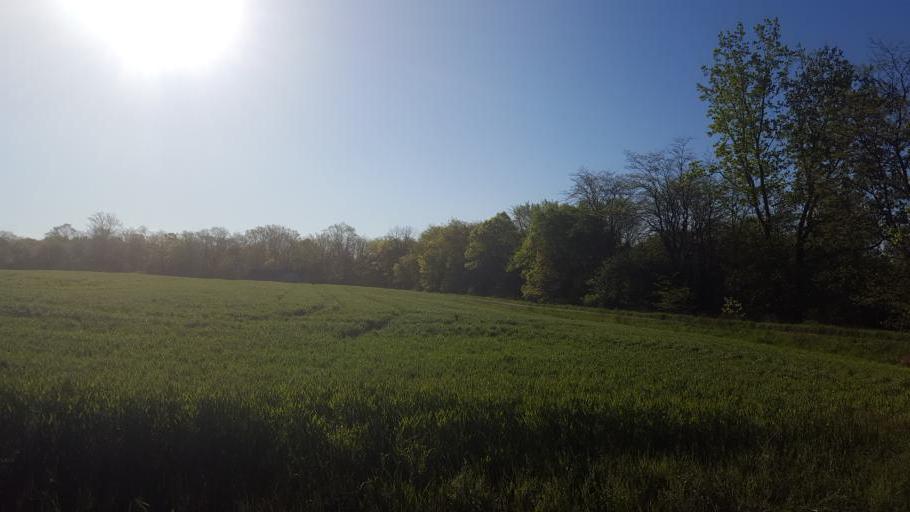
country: US
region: Ohio
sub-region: Morrow County
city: Cardington
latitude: 40.3865
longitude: -82.8138
